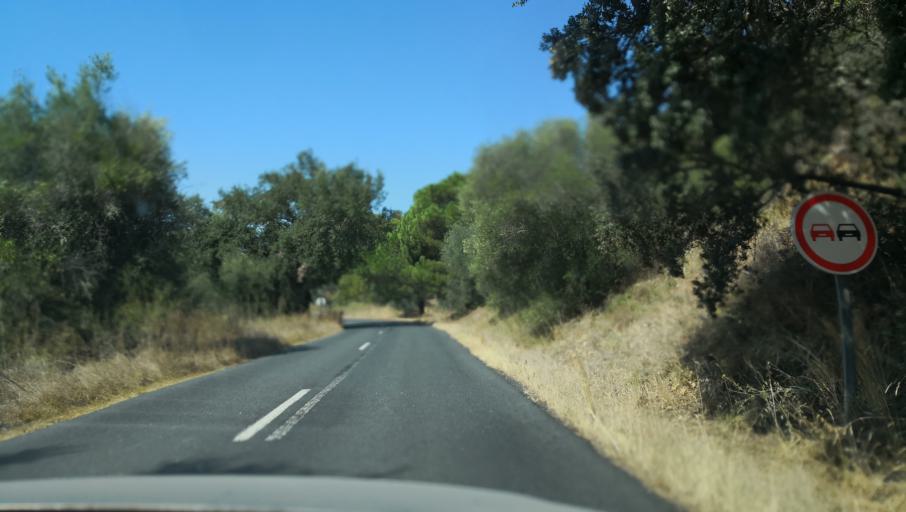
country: PT
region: Setubal
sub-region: Alcacer do Sal
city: Alcacer do Sal
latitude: 38.2787
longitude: -8.3803
